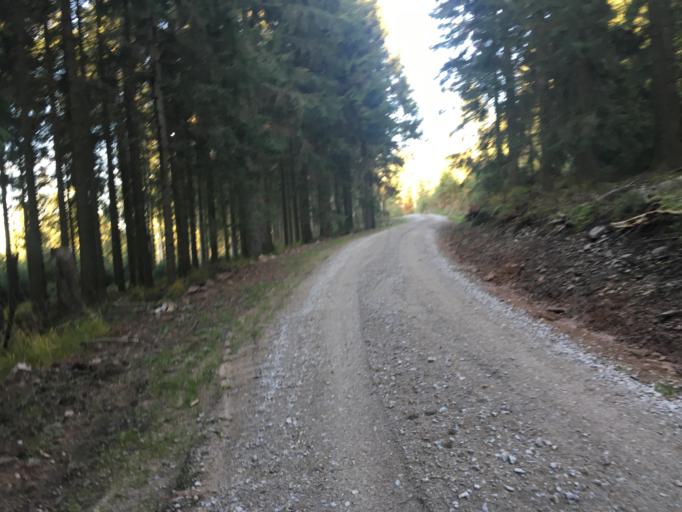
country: DE
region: Baden-Wuerttemberg
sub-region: Freiburg Region
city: Bad Peterstal-Griesbach
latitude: 48.4970
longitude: 8.2482
